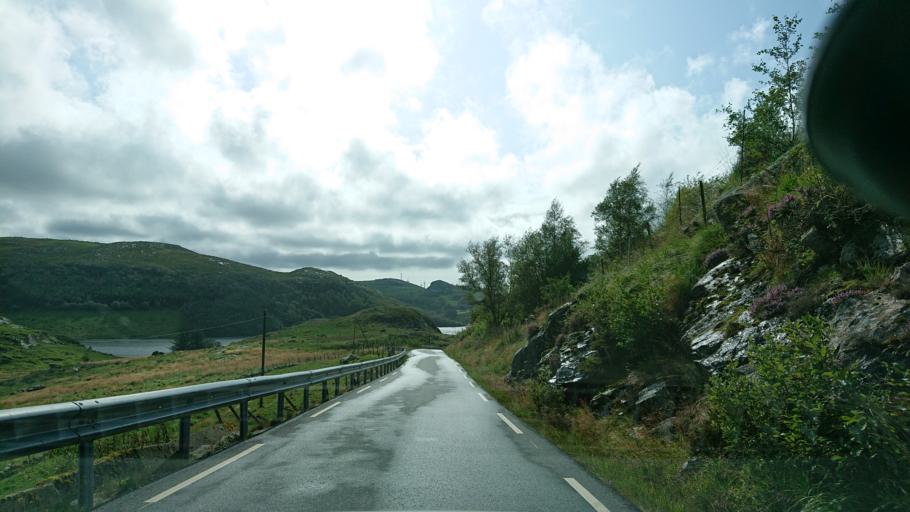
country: NO
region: Rogaland
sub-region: Gjesdal
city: Algard
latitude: 58.6785
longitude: 5.8476
